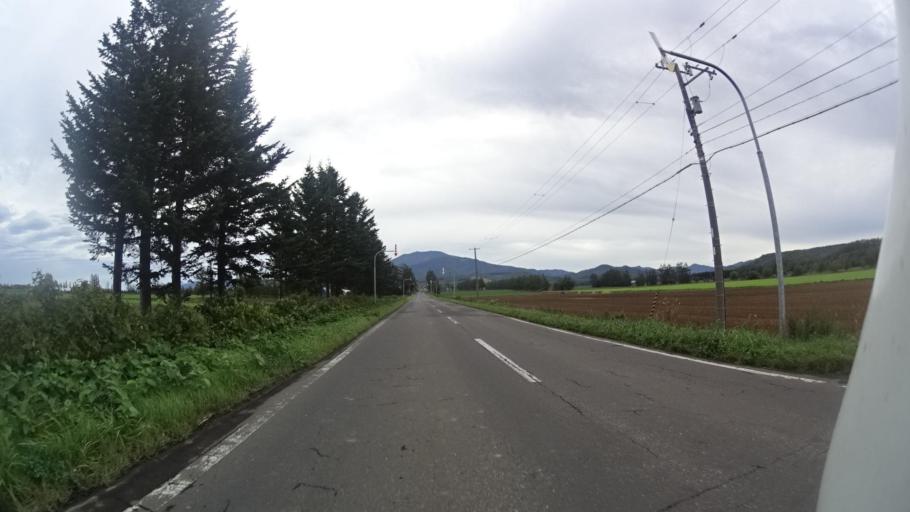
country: JP
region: Hokkaido
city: Shibetsu
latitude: 43.8735
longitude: 144.7263
